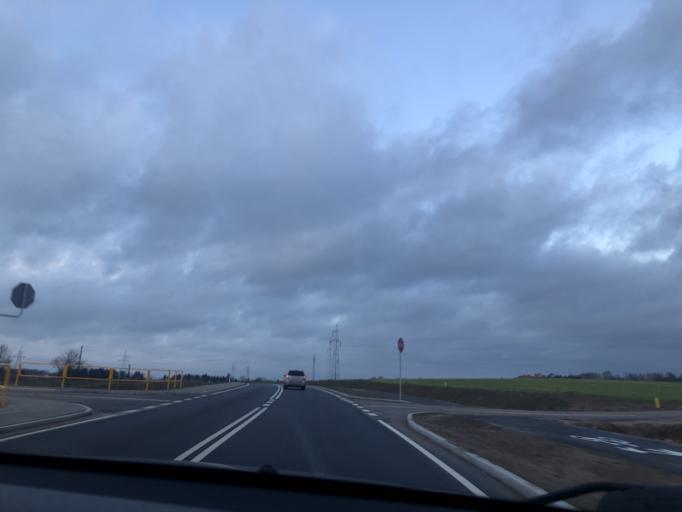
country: PL
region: Podlasie
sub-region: Lomza
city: Lomza
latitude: 53.1460
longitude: 22.0529
